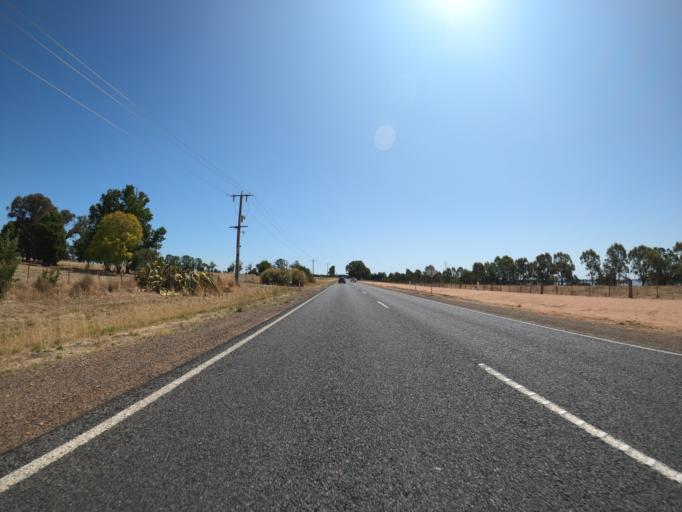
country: AU
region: Victoria
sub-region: Moira
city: Yarrawonga
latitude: -36.0270
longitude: 146.0823
